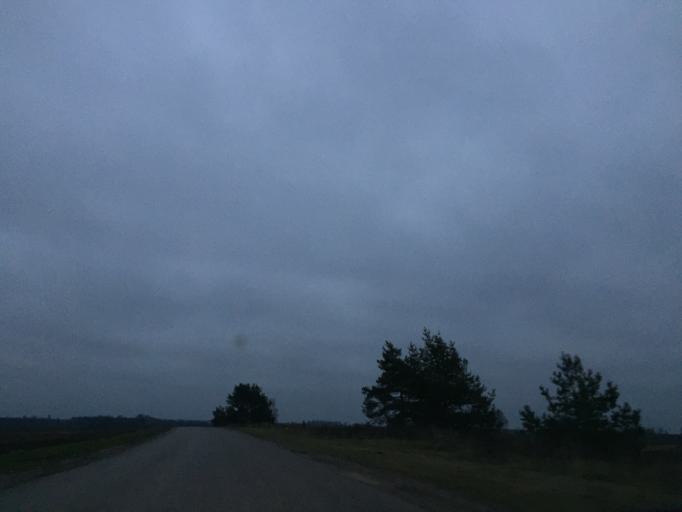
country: LV
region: Koceni
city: Koceni
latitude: 57.5499
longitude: 25.2437
